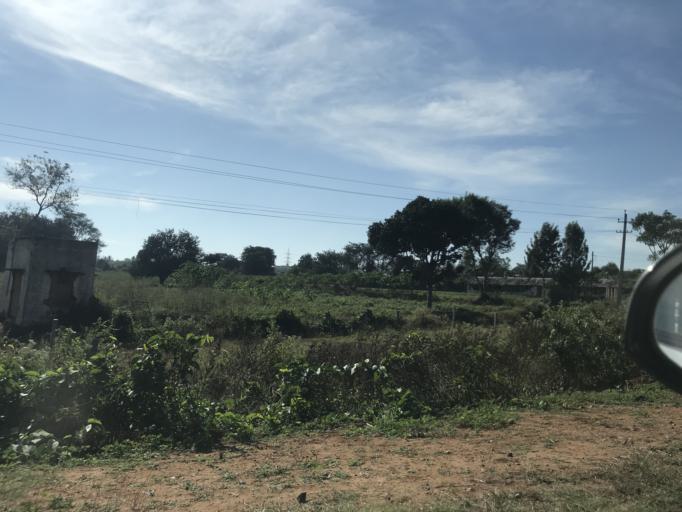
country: IN
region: Karnataka
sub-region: Mysore
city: Mysore
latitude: 12.2222
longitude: 76.5751
